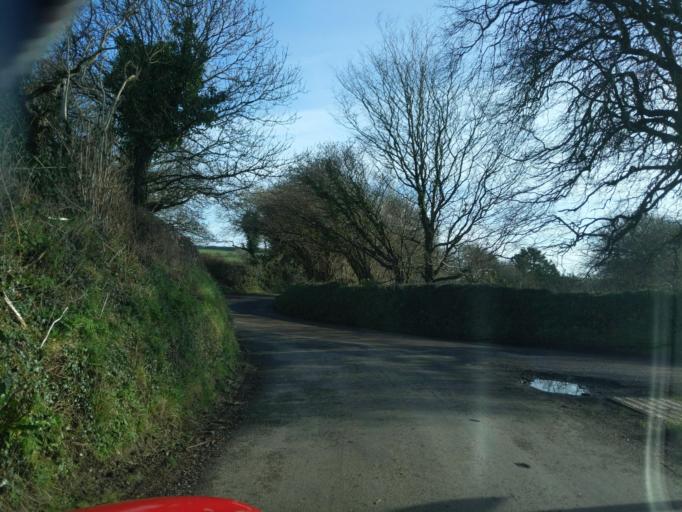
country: GB
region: England
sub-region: Devon
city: Kingsbridge
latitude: 50.3276
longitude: -3.7173
